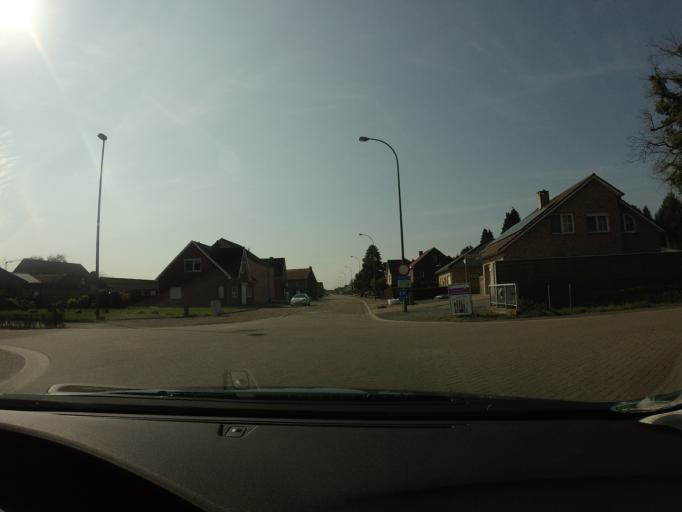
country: BE
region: Flanders
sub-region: Provincie Limburg
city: Maasmechelen
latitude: 50.9283
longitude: 5.6828
